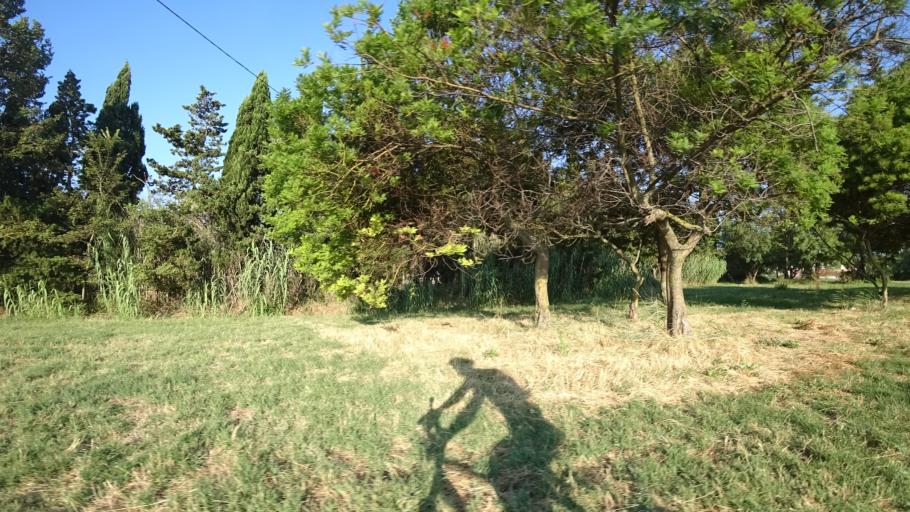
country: FR
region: Languedoc-Roussillon
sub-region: Departement des Pyrenees-Orientales
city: Sainte-Marie-Plage
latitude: 42.7312
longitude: 3.0264
